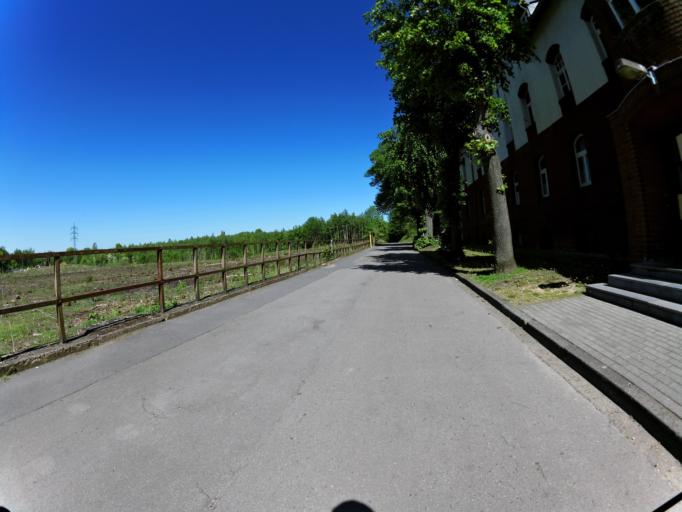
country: DE
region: North Rhine-Westphalia
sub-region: Regierungsbezirk Koln
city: Alsdorf
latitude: 50.8764
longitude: 6.1459
